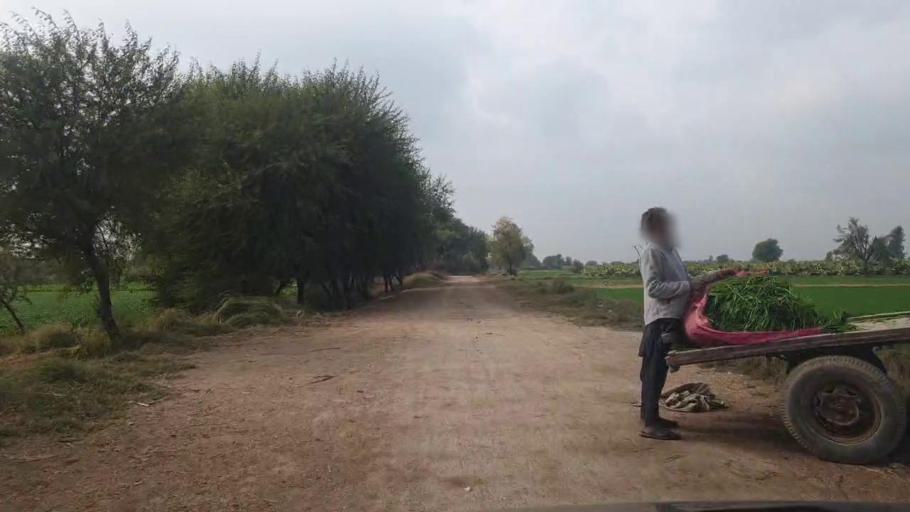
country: PK
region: Sindh
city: Shahdadpur
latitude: 25.9449
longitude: 68.7202
